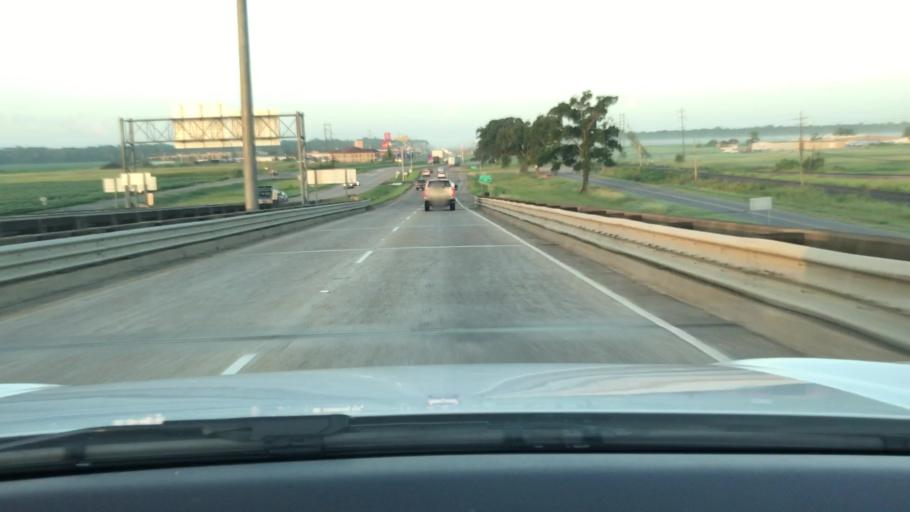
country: US
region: Louisiana
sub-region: West Baton Rouge Parish
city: Port Allen
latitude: 30.4298
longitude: -91.2129
